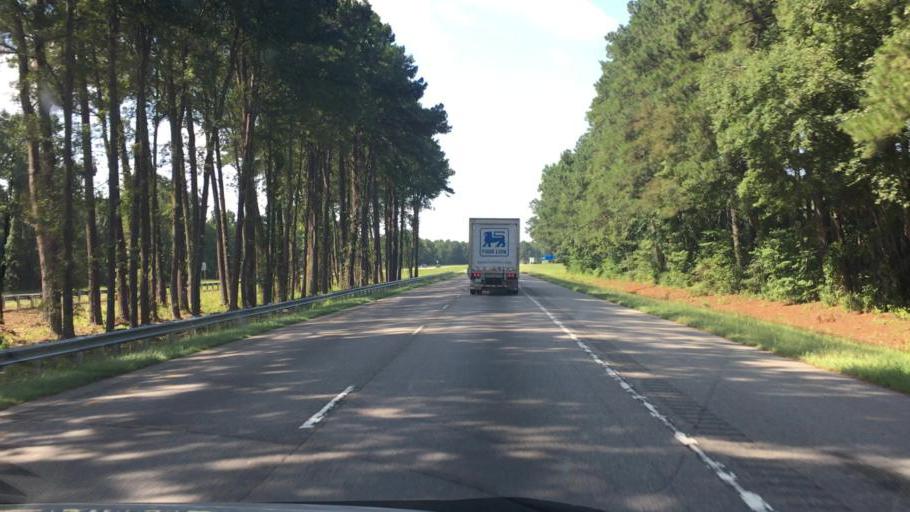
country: US
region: North Carolina
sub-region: Robeson County
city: Saint Pauls
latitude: 34.8425
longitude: -78.9726
